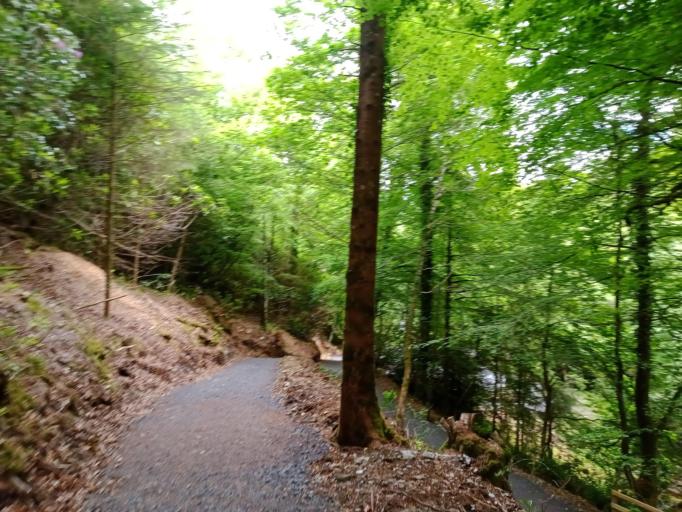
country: IE
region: Leinster
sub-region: Kilkenny
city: Thomastown
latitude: 52.4664
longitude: -7.0459
